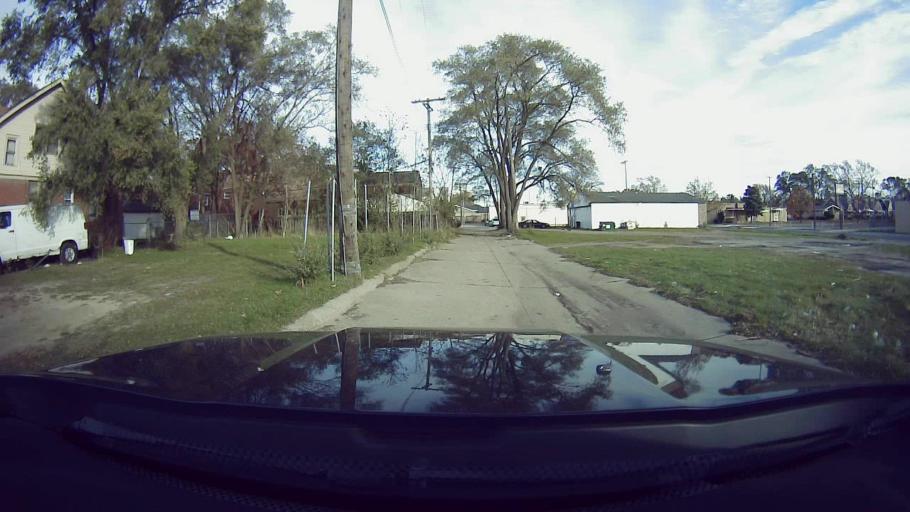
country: US
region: Michigan
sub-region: Oakland County
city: Oak Park
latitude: 42.4096
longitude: -83.1816
